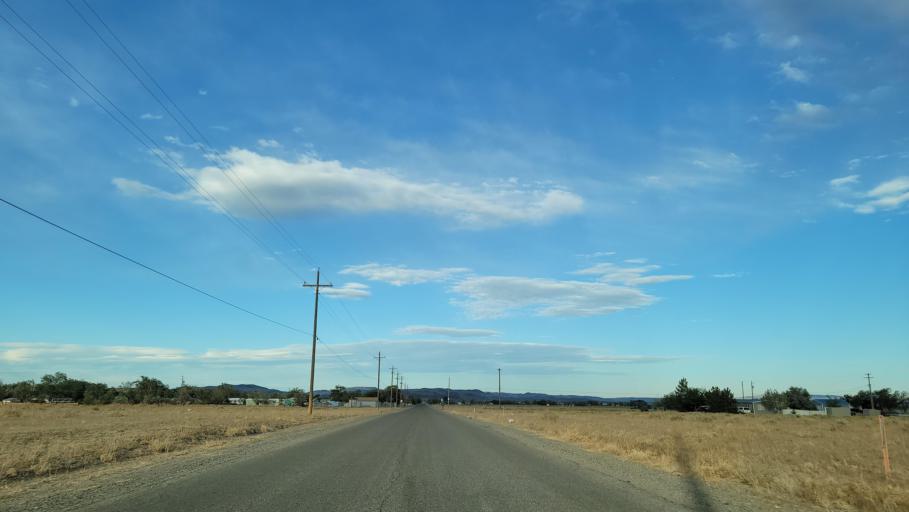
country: US
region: Nevada
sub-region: Lyon County
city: Silver Springs
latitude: 39.3899
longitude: -119.2532
